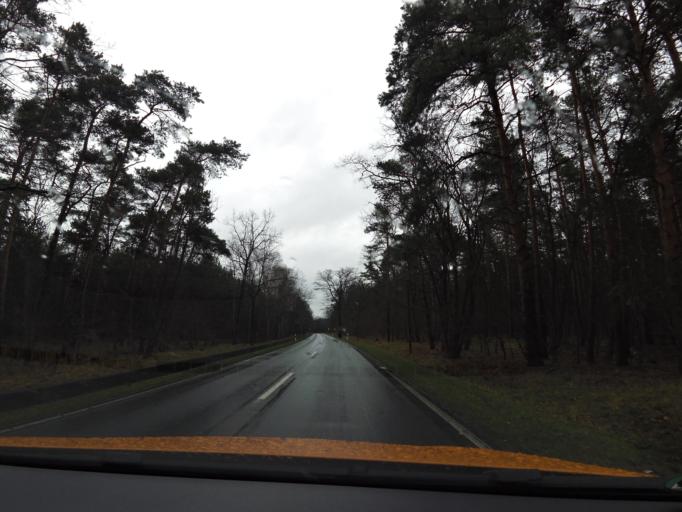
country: DE
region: Brandenburg
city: Am Mellensee
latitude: 52.1722
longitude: 13.3807
